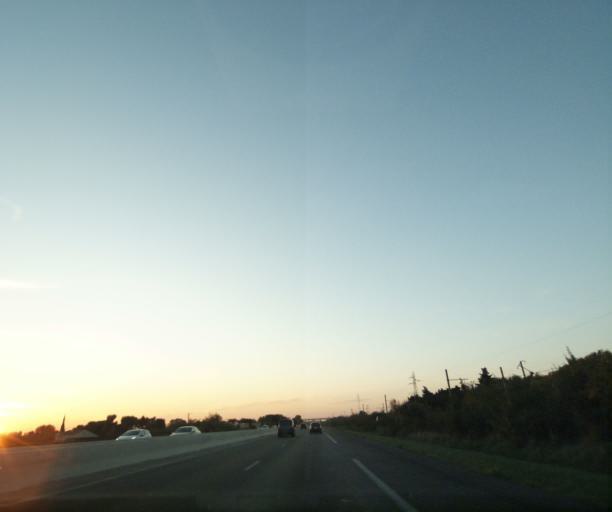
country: FR
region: Provence-Alpes-Cote d'Azur
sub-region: Departement des Bouches-du-Rhone
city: Arles
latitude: 43.6510
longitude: 4.6739
